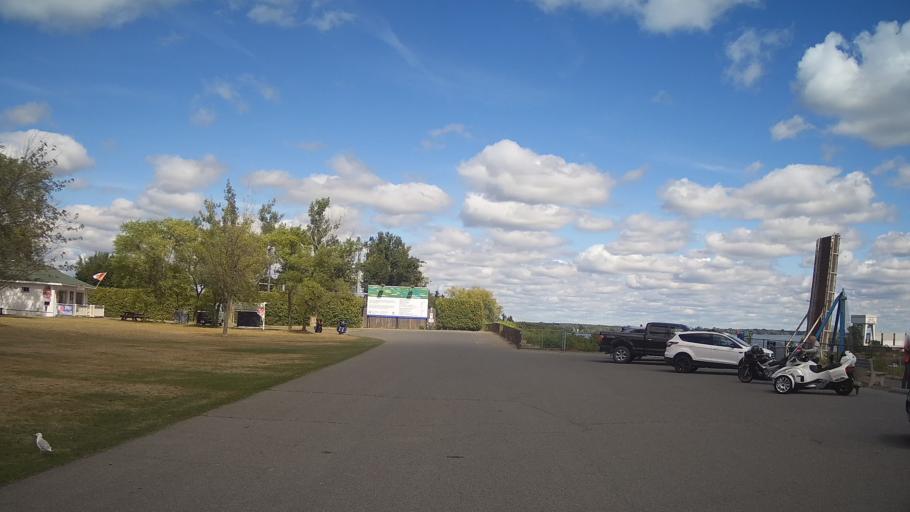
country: US
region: New York
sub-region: St. Lawrence County
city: Ogdensburg
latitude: 44.8316
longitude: -75.3133
